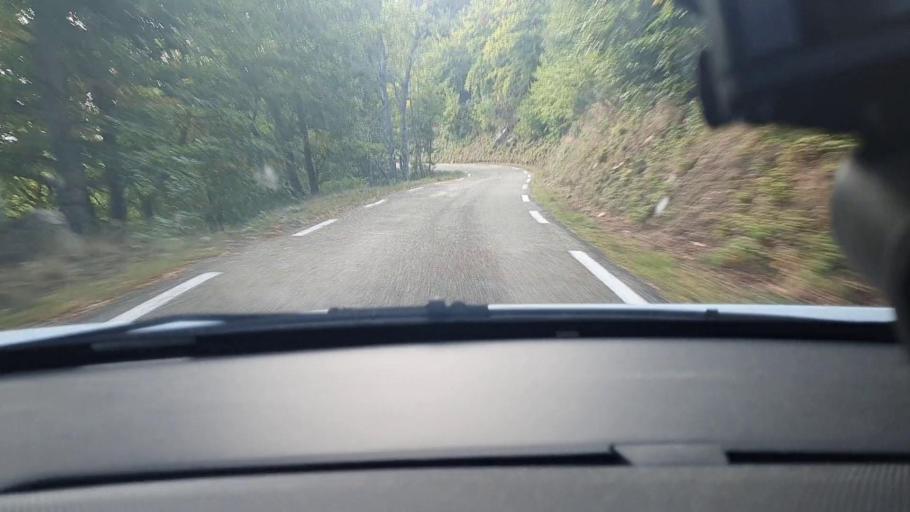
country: FR
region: Languedoc-Roussillon
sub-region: Departement du Gard
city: Branoux-les-Taillades
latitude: 44.3657
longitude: 3.9152
